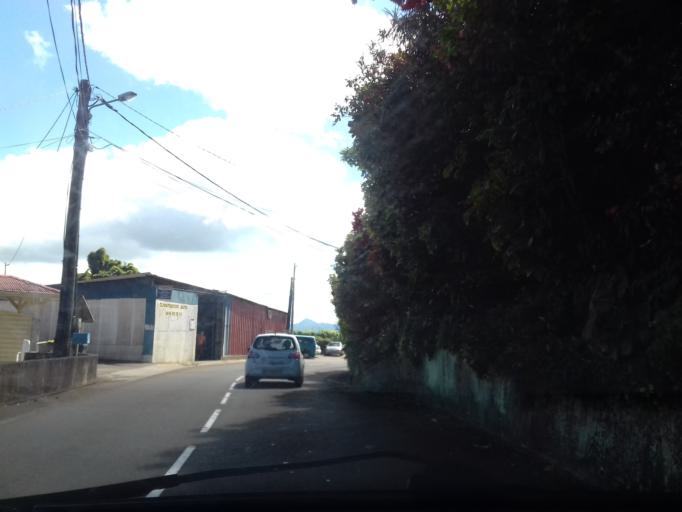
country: MQ
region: Martinique
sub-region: Martinique
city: Saint-Joseph
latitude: 14.6691
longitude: -61.0491
